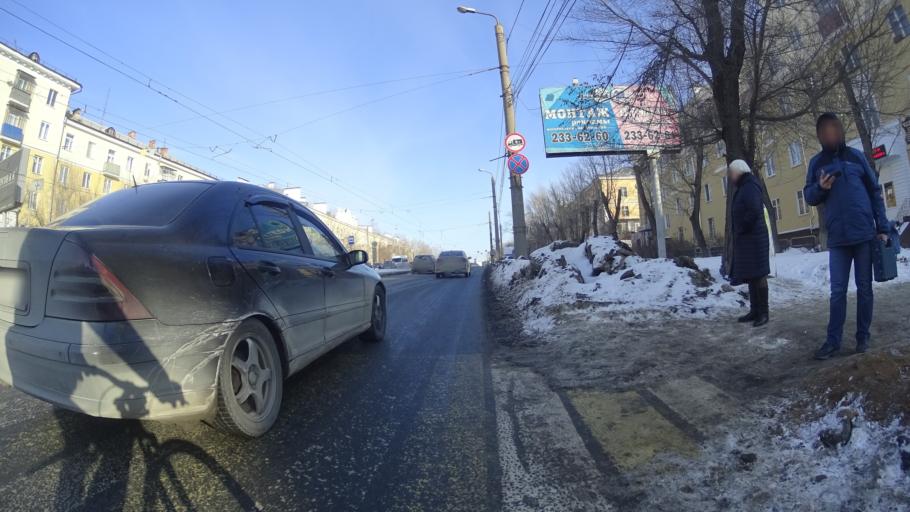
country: RU
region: Chelyabinsk
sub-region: Gorod Chelyabinsk
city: Chelyabinsk
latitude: 55.1854
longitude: 61.4205
